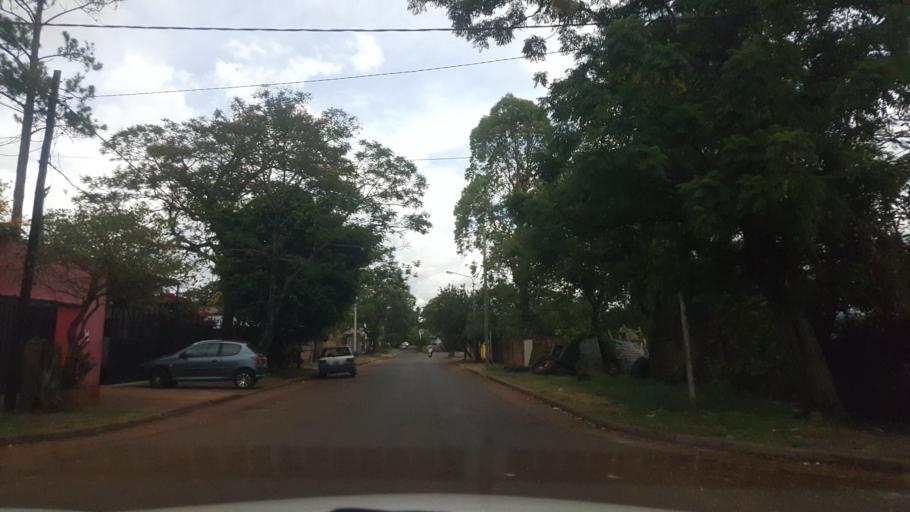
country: AR
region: Misiones
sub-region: Departamento de Capital
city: Posadas
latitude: -27.4012
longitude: -55.8937
